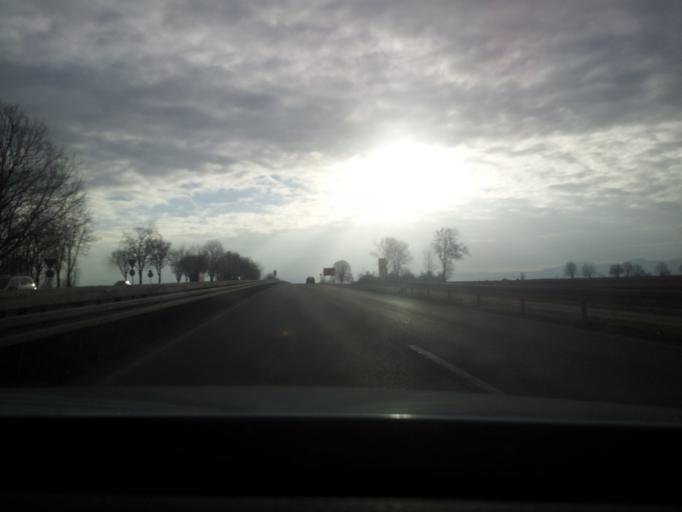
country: DE
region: Baden-Wuerttemberg
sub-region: Tuebingen Region
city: Kusterdingen
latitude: 48.5073
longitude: 9.1027
